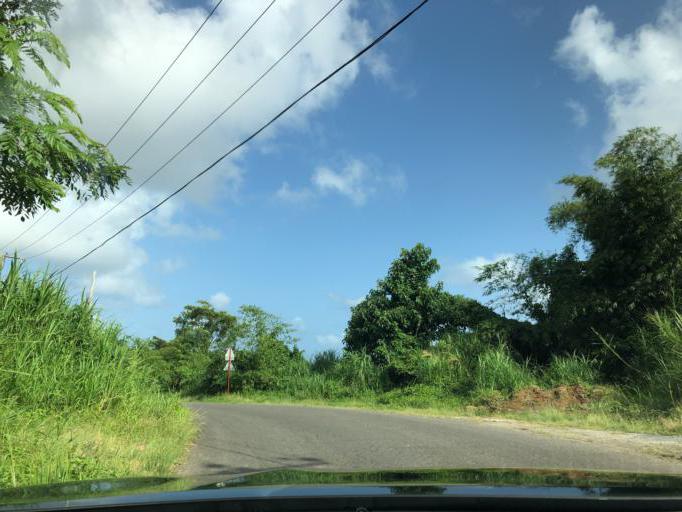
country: LC
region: Castries Quarter
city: Bisee
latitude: 13.9937
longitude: -60.9679
